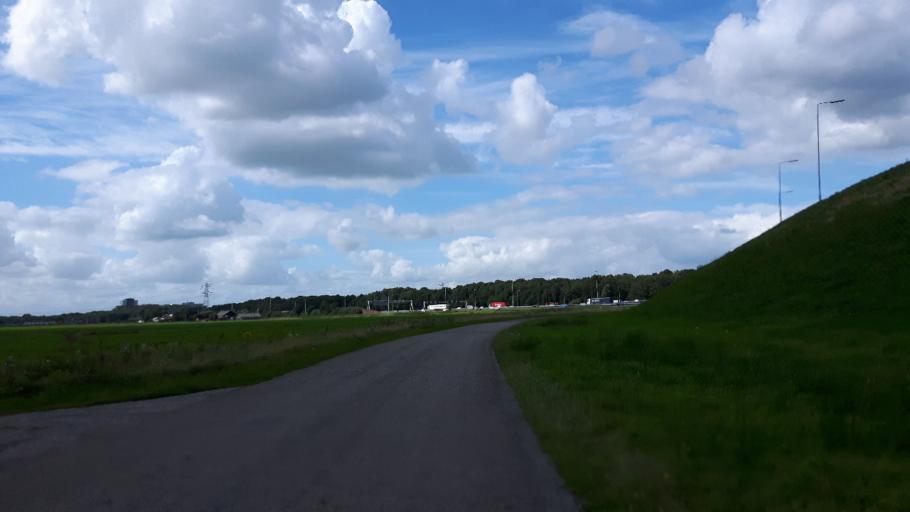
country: NL
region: Utrecht
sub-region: Gemeente Nieuwegein
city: Nieuwegein
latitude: 52.0641
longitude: 5.0649
